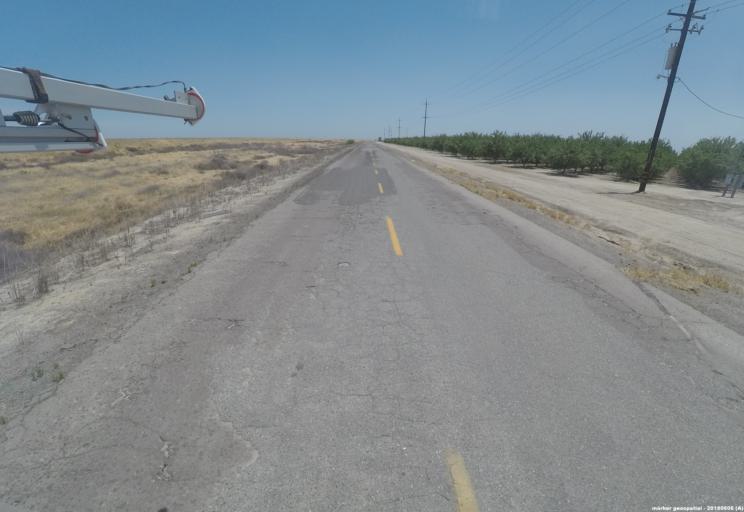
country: US
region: California
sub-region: Fresno County
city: Mendota
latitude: 36.8032
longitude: -120.3101
